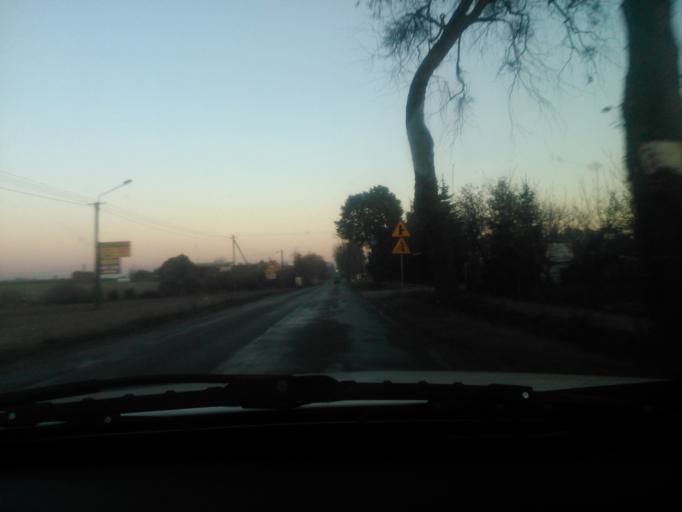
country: PL
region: Kujawsko-Pomorskie
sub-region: Powiat golubsko-dobrzynski
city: Golub-Dobrzyn
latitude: 53.1414
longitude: 18.9884
